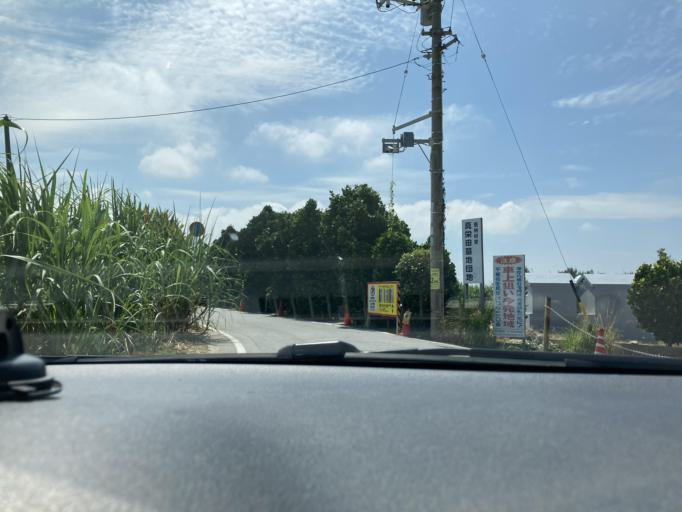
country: JP
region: Okinawa
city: Ishikawa
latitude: 26.4426
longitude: 127.7700
